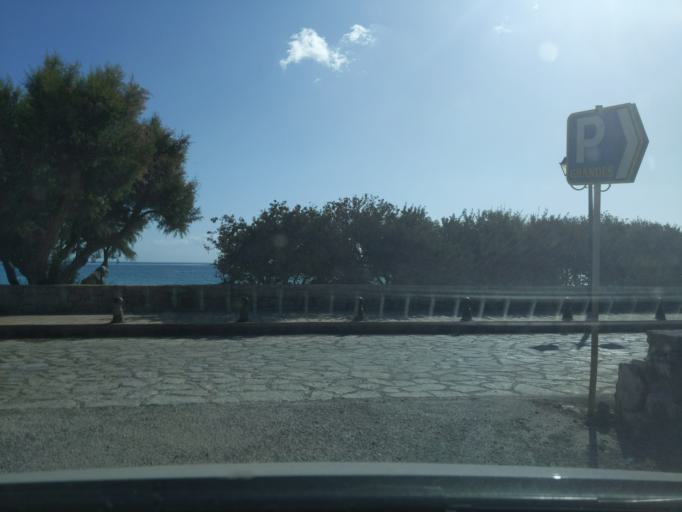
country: GR
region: Crete
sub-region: Nomos Lasithiou
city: Palekastro
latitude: 35.2121
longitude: 26.2673
